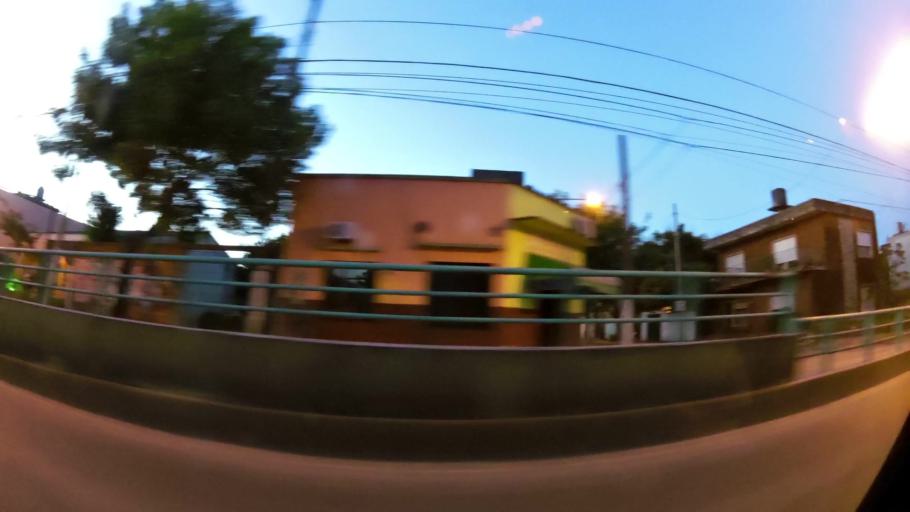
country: AR
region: Buenos Aires
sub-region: Partido de Quilmes
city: Quilmes
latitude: -34.7669
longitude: -58.2011
